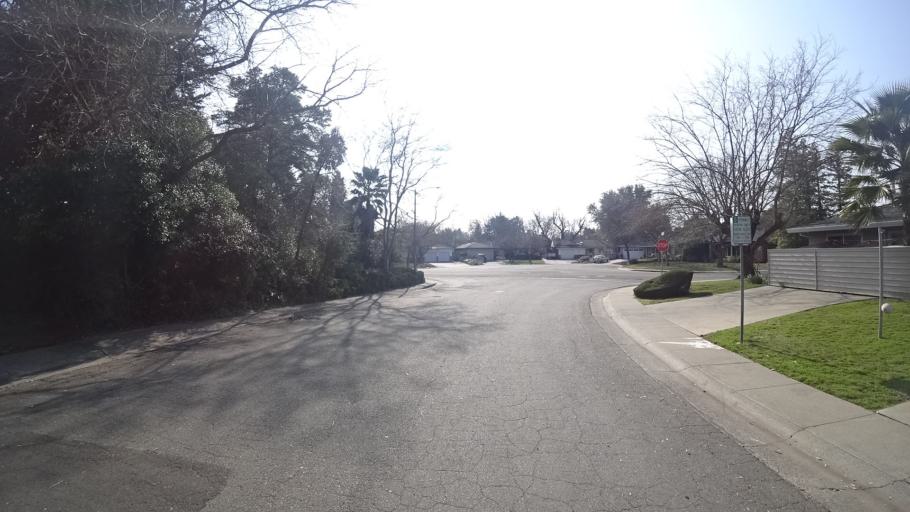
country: US
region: California
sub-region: Yolo County
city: Davis
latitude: 38.5544
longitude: -121.7511
